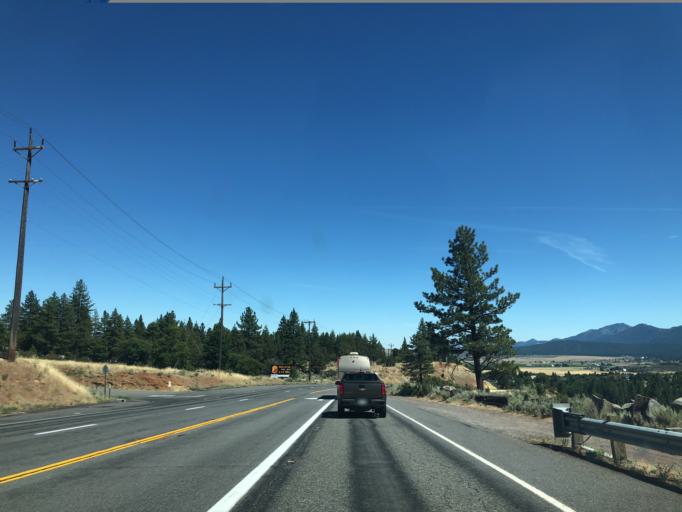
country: US
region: California
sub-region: Lassen County
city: Susanville
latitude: 40.4217
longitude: -120.6741
